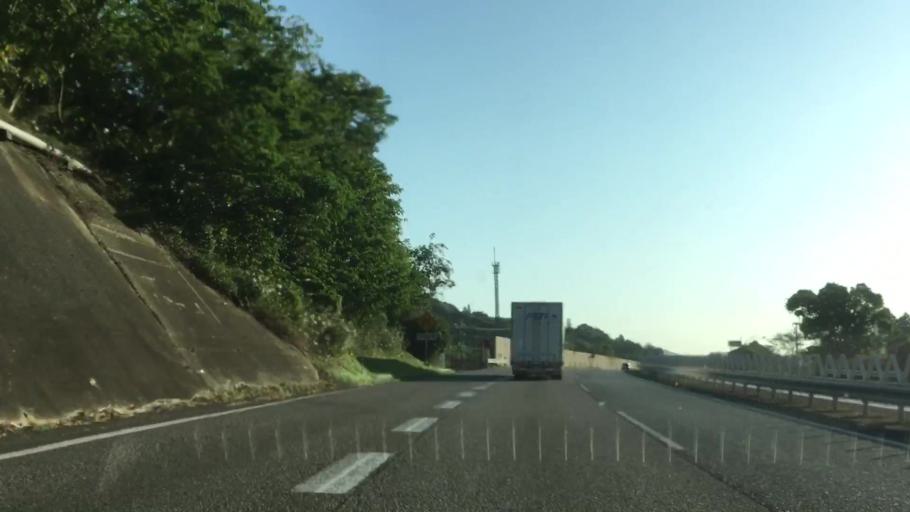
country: JP
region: Yamaguchi
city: Onoda
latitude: 34.1473
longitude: 131.2335
